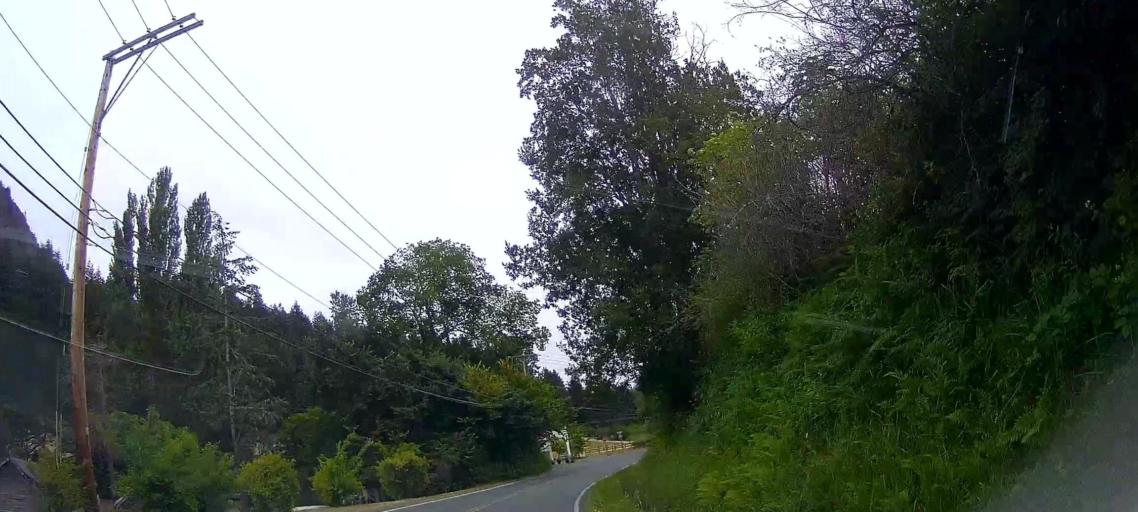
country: US
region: Washington
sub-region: Skagit County
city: Anacortes
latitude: 48.4495
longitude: -122.6346
